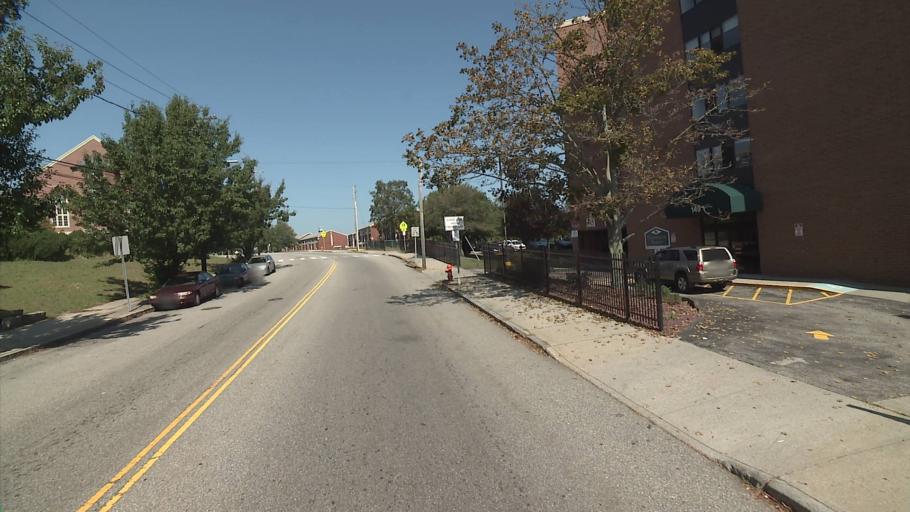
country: US
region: Connecticut
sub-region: New London County
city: New London
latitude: 41.3577
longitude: -72.0993
